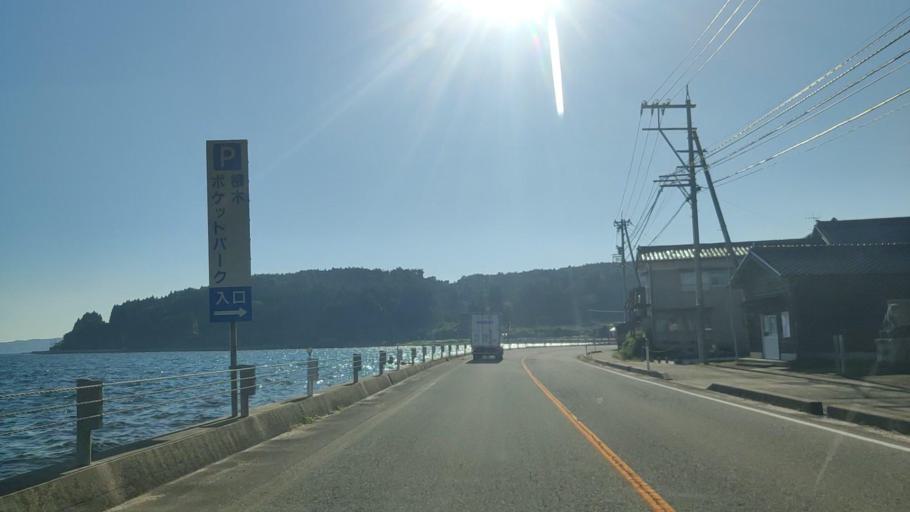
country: JP
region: Ishikawa
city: Nanao
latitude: 37.1922
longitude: 136.9090
